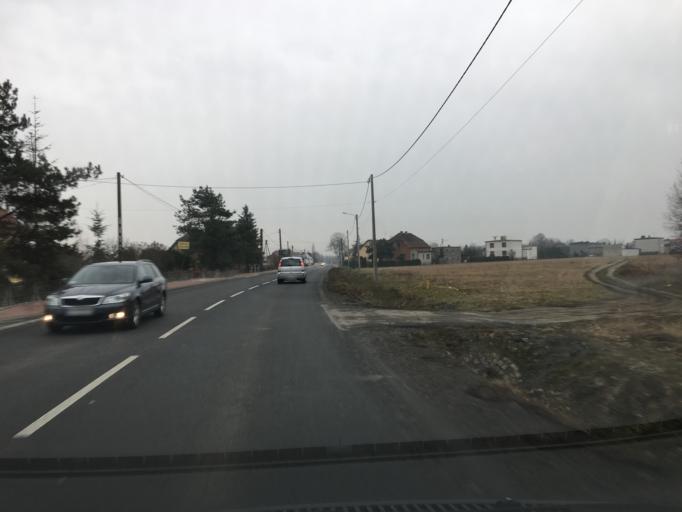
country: PL
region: Opole Voivodeship
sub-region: Powiat kedzierzynsko-kozielski
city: Kedzierzyn-Kozle
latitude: 50.3178
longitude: 18.2239
